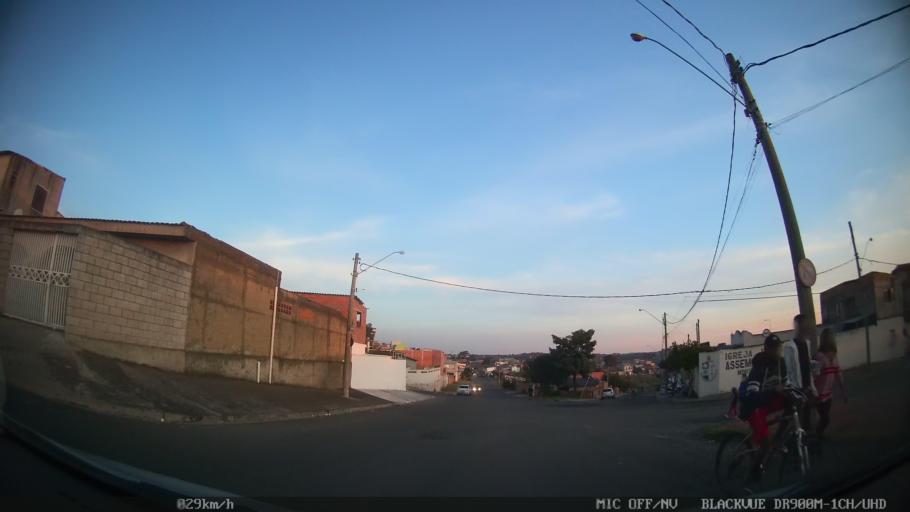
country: BR
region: Sao Paulo
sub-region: Campinas
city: Campinas
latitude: -22.9831
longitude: -47.1234
